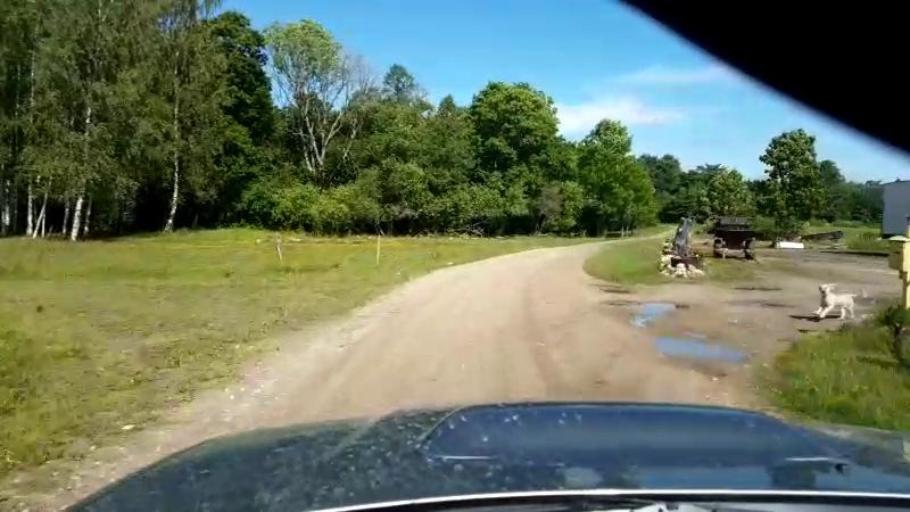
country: EE
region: Paernumaa
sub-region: Sindi linn
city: Sindi
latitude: 58.5159
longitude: 24.6632
